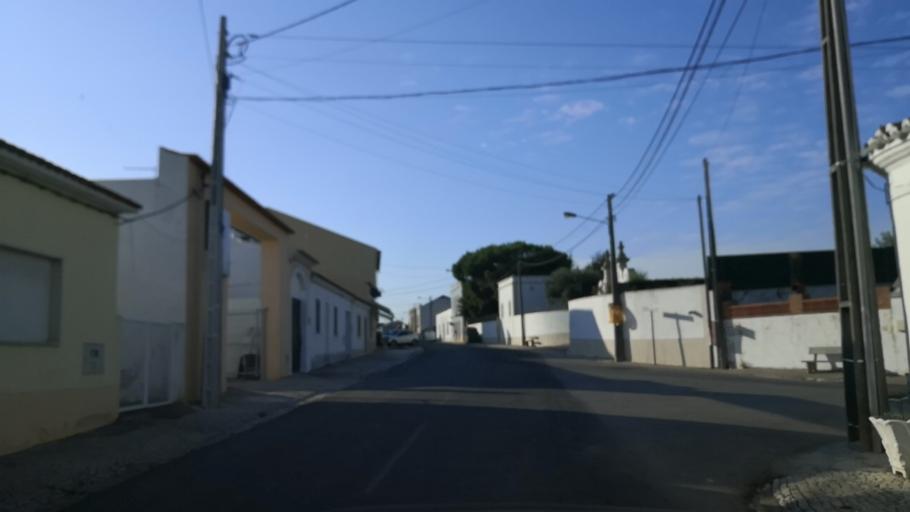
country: PT
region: Santarem
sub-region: Santarem
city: Santarem
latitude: 39.2927
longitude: -8.6546
